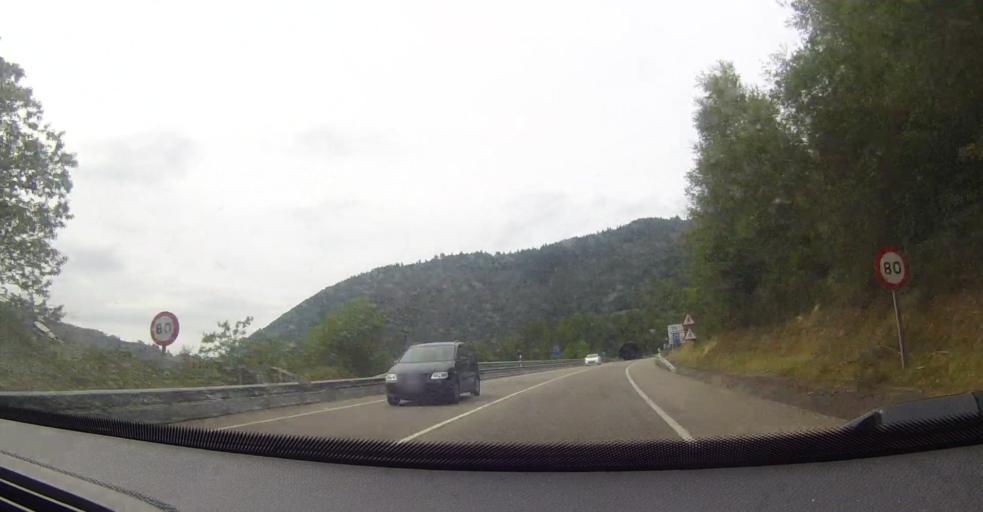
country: ES
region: Asturias
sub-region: Province of Asturias
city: Pilona
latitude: 43.3477
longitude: -5.3609
